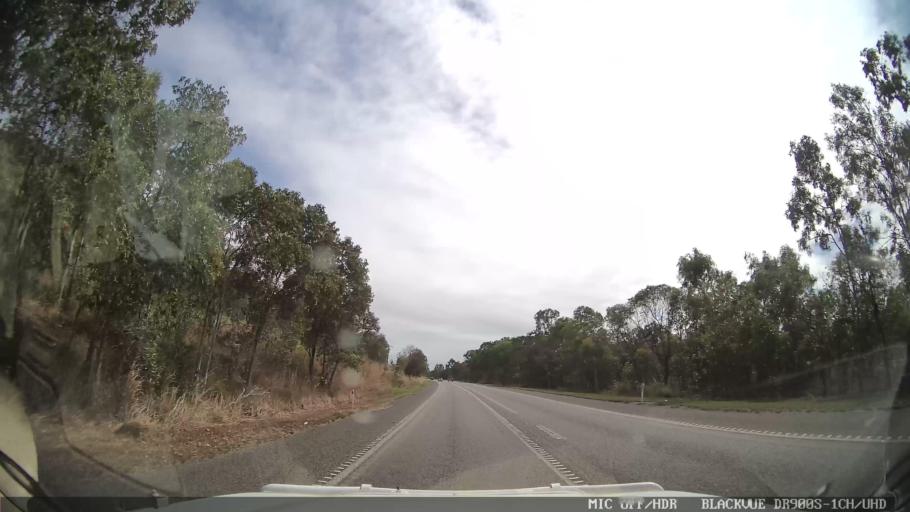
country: AU
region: Queensland
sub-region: Hinchinbrook
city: Ingham
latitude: -19.0105
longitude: 146.3636
